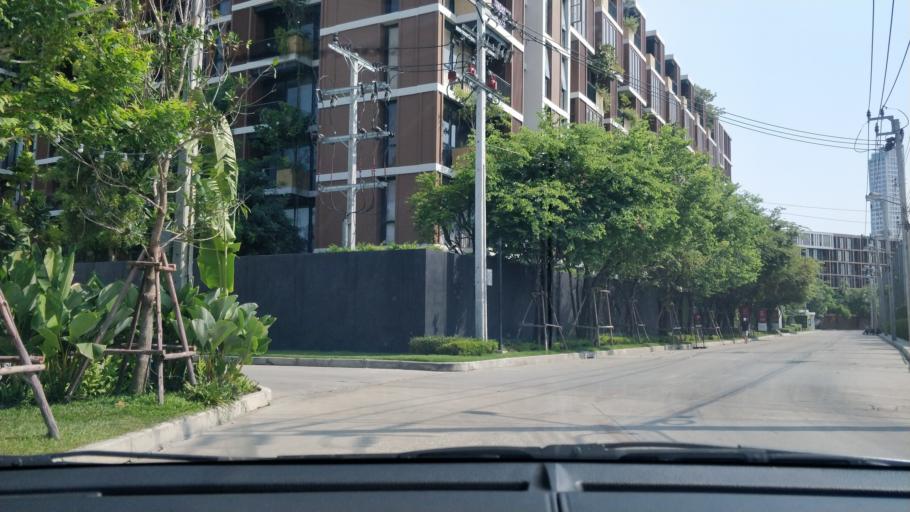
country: TH
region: Bangkok
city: Phra Khanong
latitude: 13.7159
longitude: 100.6027
